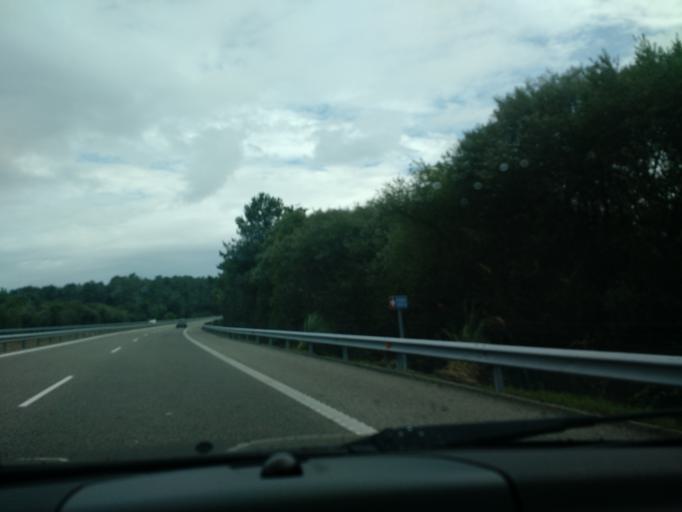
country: ES
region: Galicia
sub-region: Provincia da Coruna
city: Abegondo
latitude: 43.2226
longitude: -8.2746
